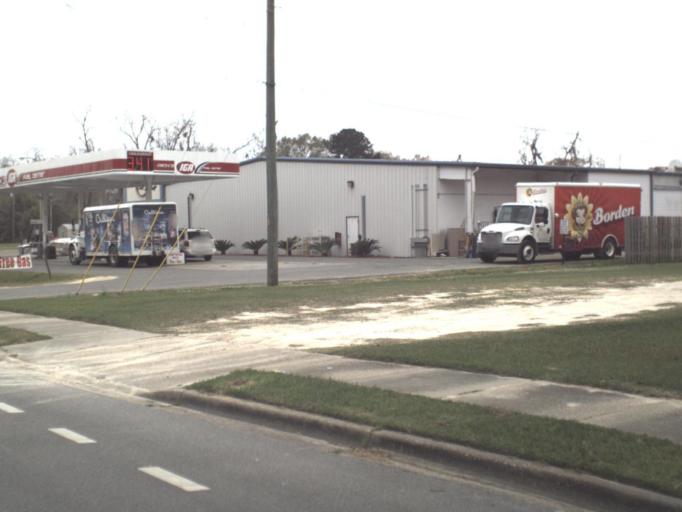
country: US
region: Florida
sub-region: Gulf County
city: Wewahitchka
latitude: 30.1072
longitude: -85.2005
